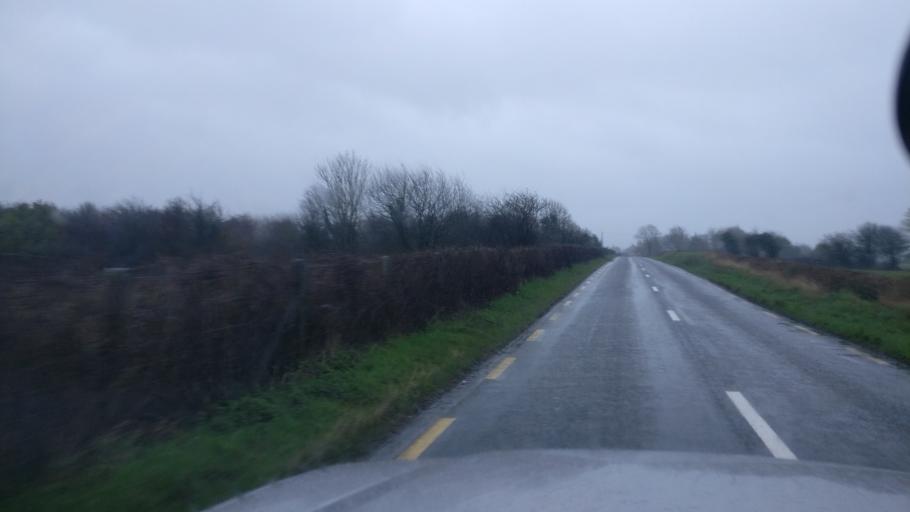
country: IE
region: Connaught
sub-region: County Galway
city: Ballinasloe
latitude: 53.2747
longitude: -8.2060
